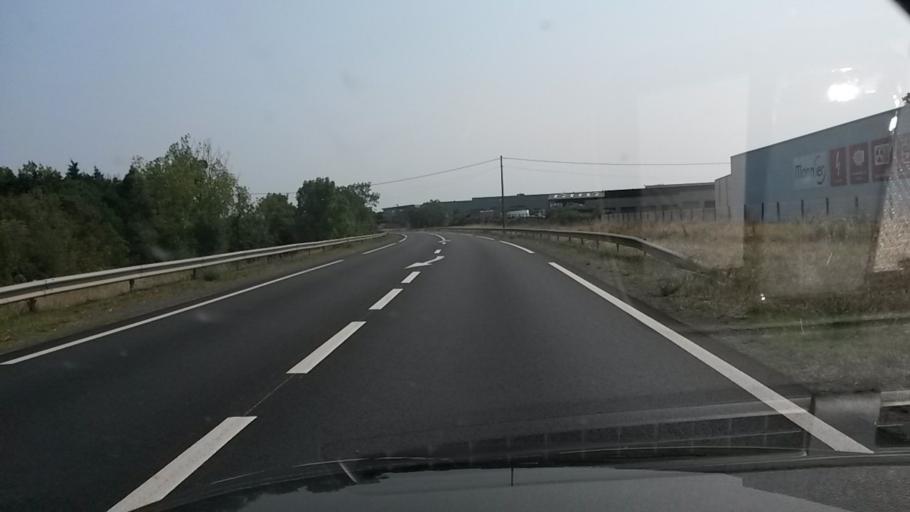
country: FR
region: Pays de la Loire
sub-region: Departement de la Loire-Atlantique
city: Ancenis
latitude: 47.3800
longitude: -1.1726
